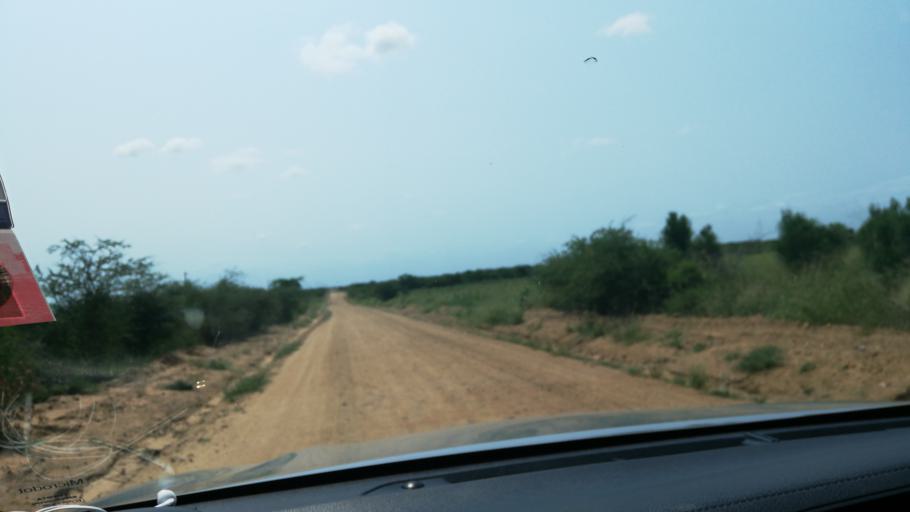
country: MZ
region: Maputo
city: Matola
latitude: -26.0816
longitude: 32.3913
